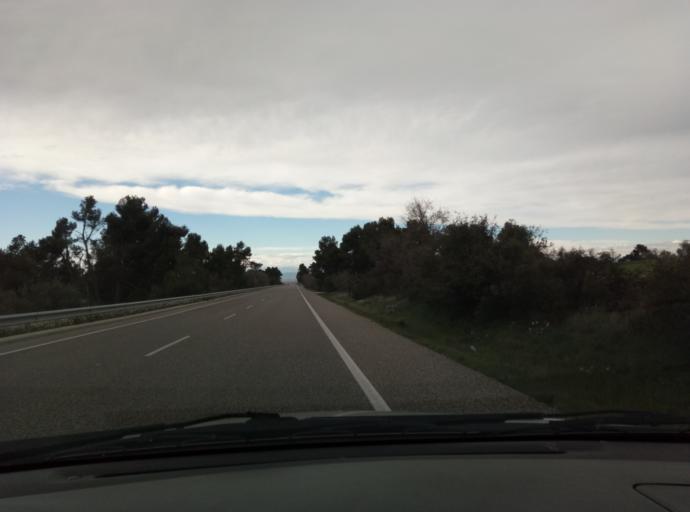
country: ES
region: Catalonia
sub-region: Provincia de Lleida
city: Ciutadilla
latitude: 41.5356
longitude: 1.1516
